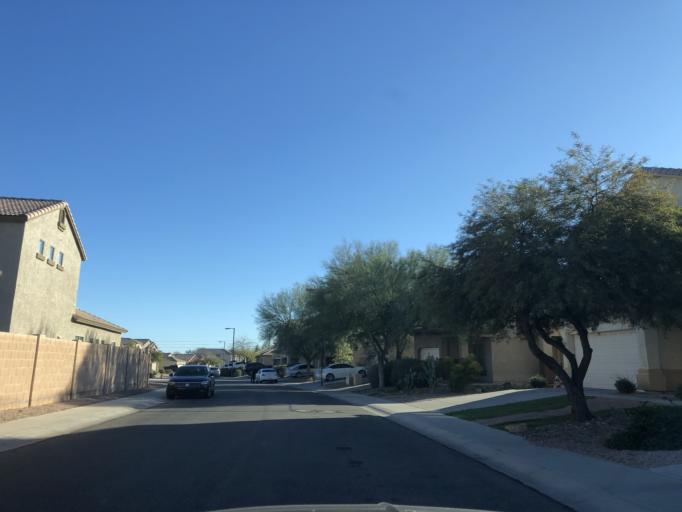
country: US
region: Arizona
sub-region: Maricopa County
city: Buckeye
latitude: 33.4382
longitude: -112.5682
